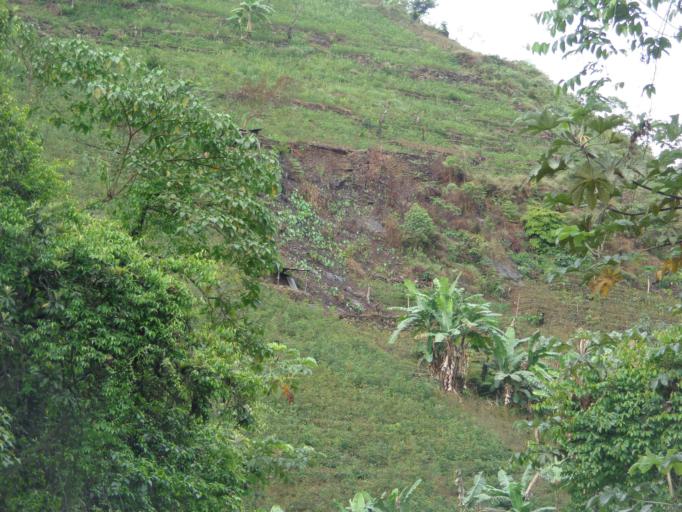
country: BO
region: La Paz
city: Coripata
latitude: -16.3943
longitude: -67.6992
